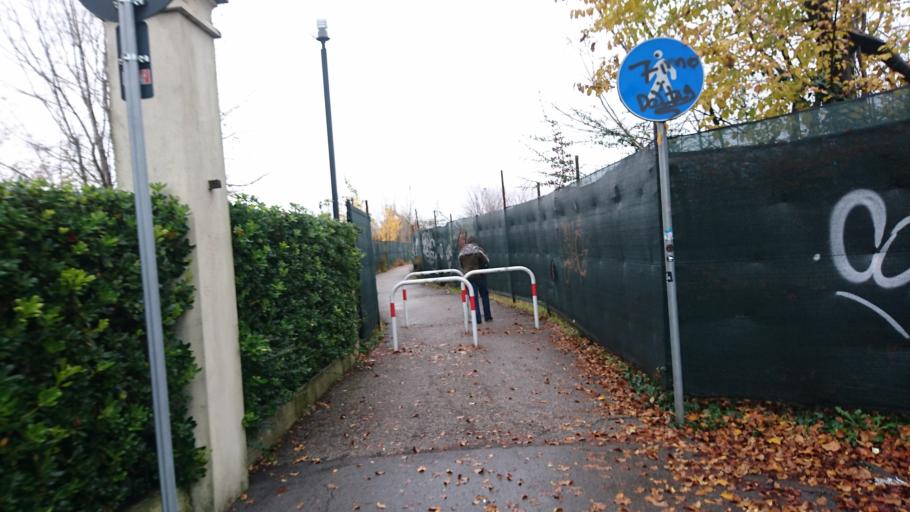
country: IT
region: Veneto
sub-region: Provincia di Treviso
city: Castelfranco Veneto
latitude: 45.6678
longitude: 11.9356
